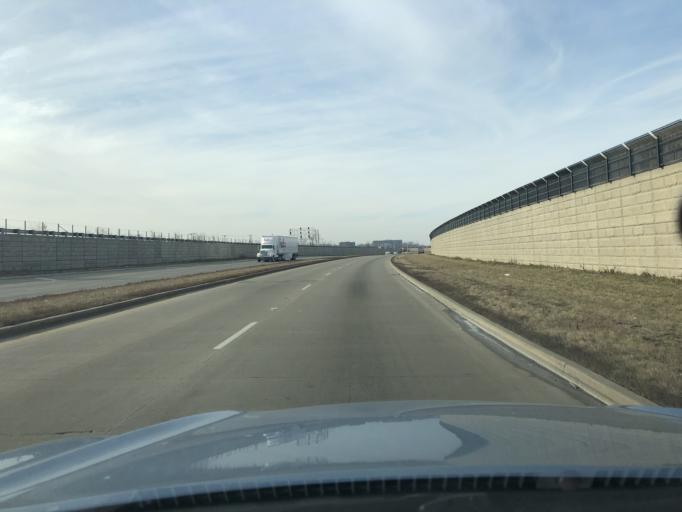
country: US
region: Illinois
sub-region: DuPage County
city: Bensenville
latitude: 41.9552
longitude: -87.9263
